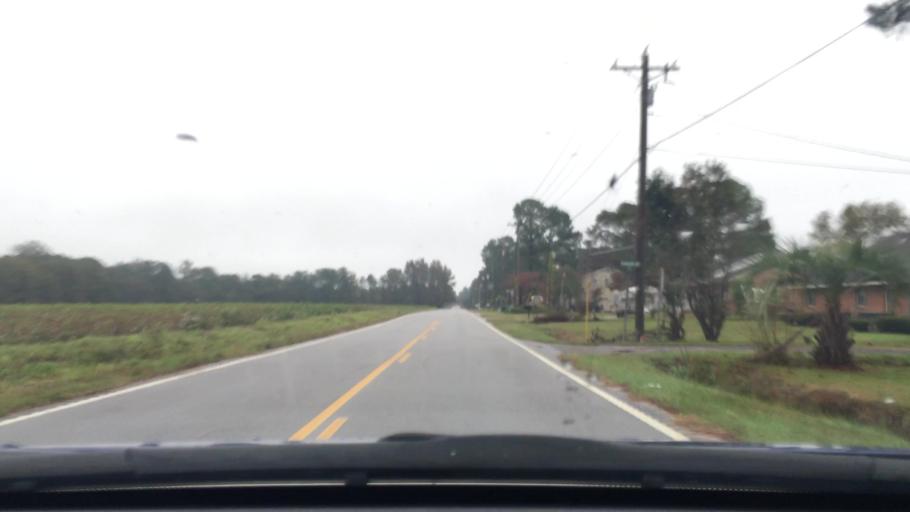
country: US
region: South Carolina
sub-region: Darlington County
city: Darlington
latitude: 34.2905
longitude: -79.9197
